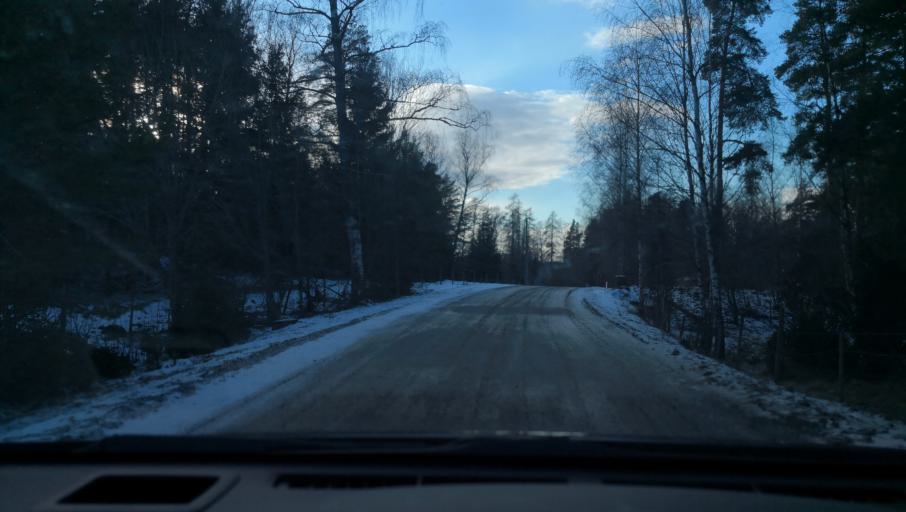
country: SE
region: Uppsala
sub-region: Enkopings Kommun
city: Irsta
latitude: 59.6591
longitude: 16.7876
